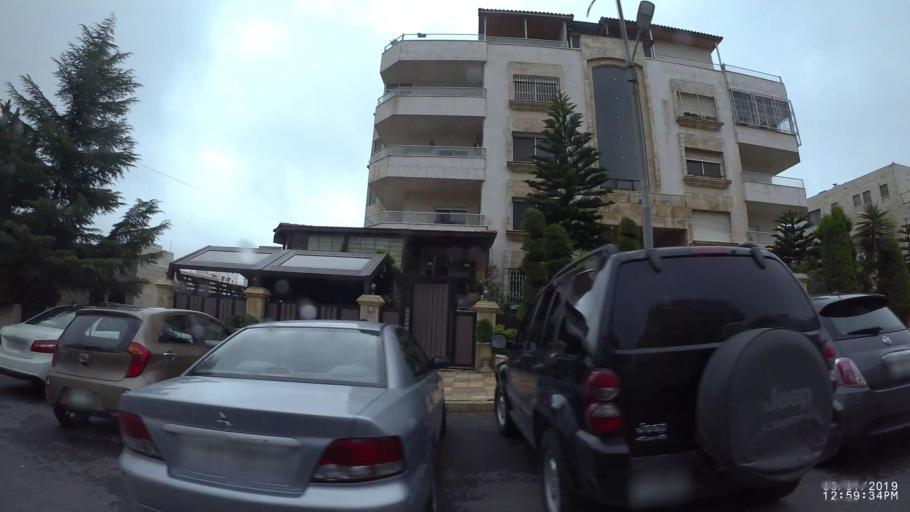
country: JO
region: Amman
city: Wadi as Sir
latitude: 31.9384
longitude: 35.8649
